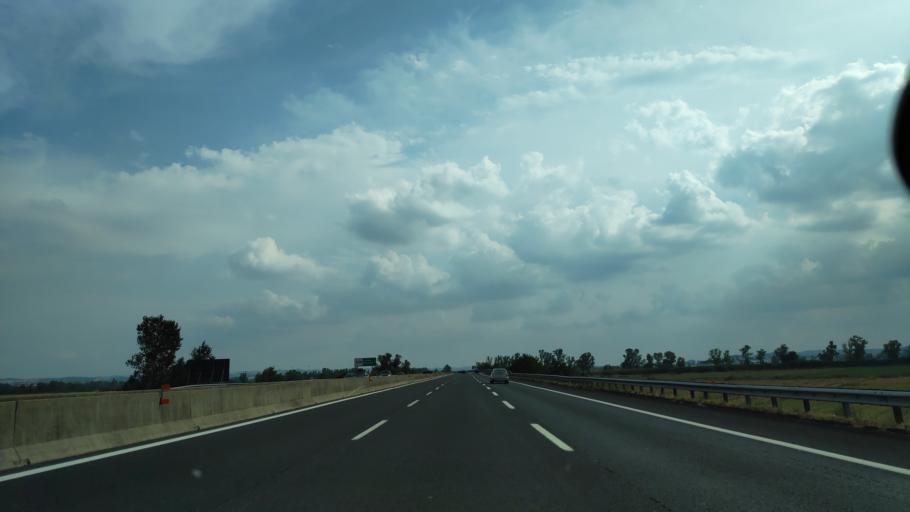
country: IT
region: Latium
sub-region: Citta metropolitana di Roma Capitale
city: Fiano Romano
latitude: 42.1383
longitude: 12.6198
